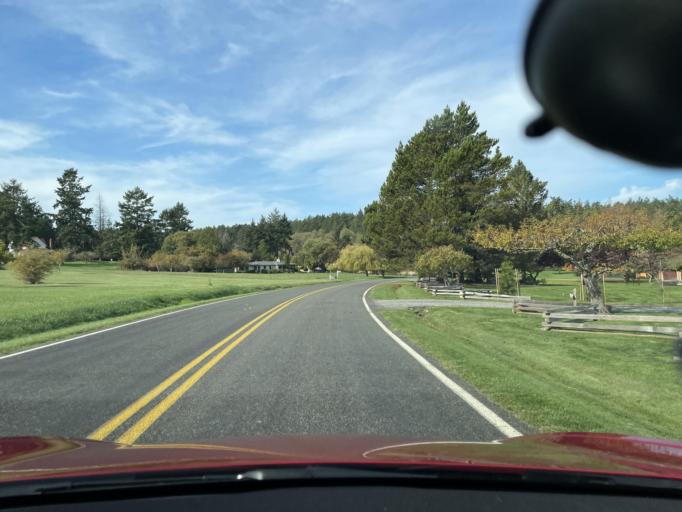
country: US
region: Washington
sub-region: San Juan County
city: Friday Harbor
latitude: 48.5269
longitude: -122.9801
